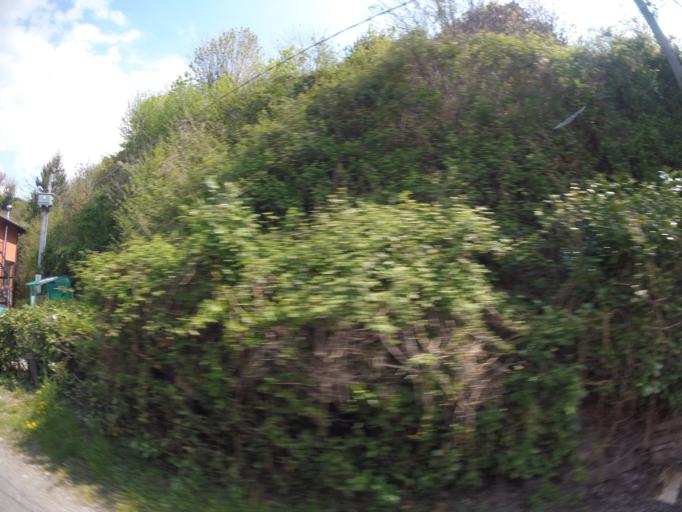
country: IT
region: Piedmont
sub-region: Provincia di Novara
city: Pettenasco
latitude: 45.8290
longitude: 8.3972
